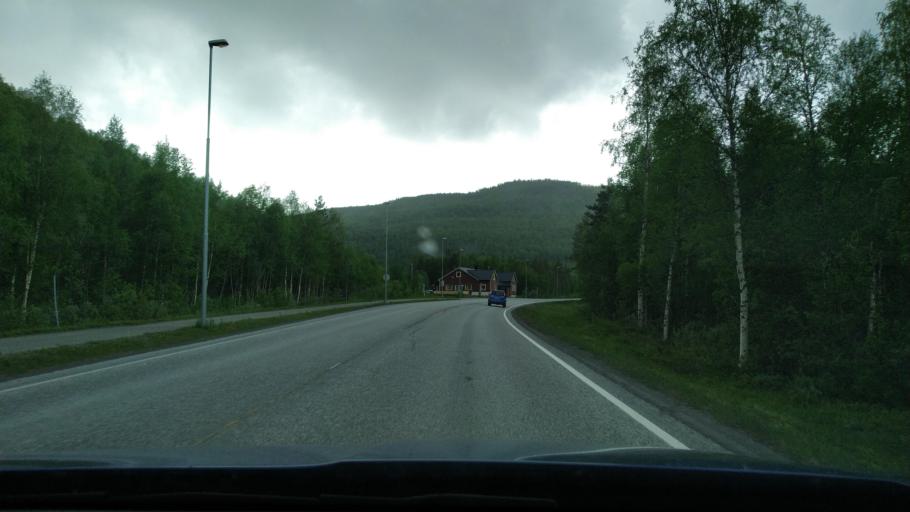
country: NO
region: Troms
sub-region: Malselv
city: Moen
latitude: 69.0093
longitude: 18.4985
